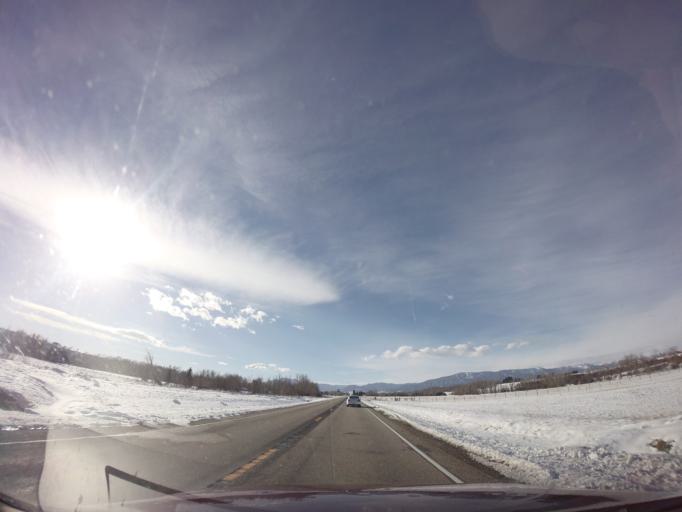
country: US
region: Montana
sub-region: Carbon County
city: Red Lodge
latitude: 45.2854
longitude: -109.2125
